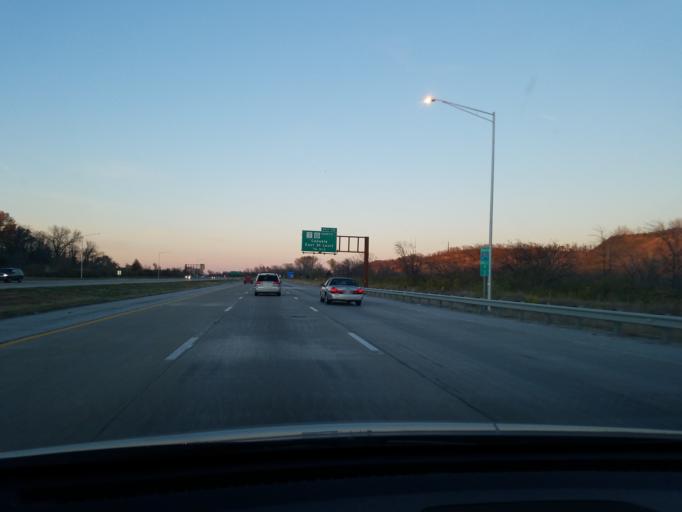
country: US
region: Illinois
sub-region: Saint Clair County
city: Dupo
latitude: 38.5092
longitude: -90.2045
